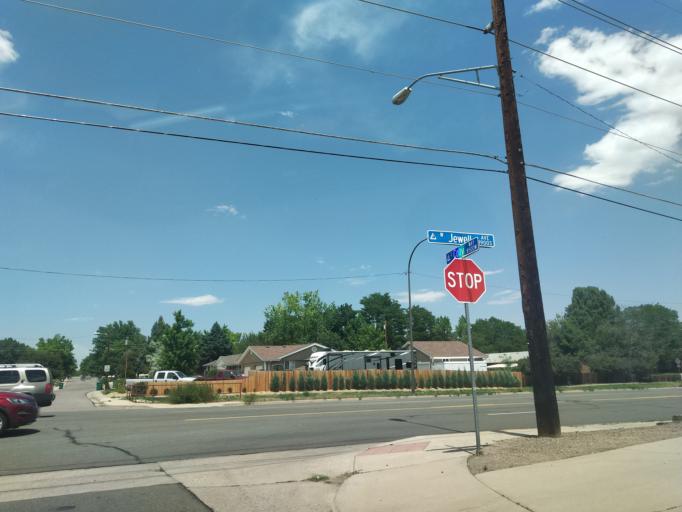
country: US
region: Colorado
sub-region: Jefferson County
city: Lakewood
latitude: 39.6820
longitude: -105.0919
